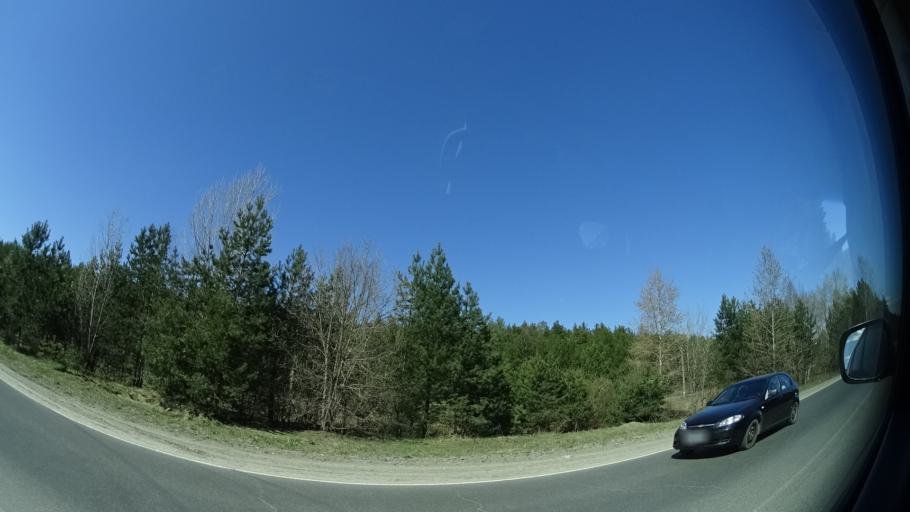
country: RU
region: Perm
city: Perm
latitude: 58.0662
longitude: 56.2745
